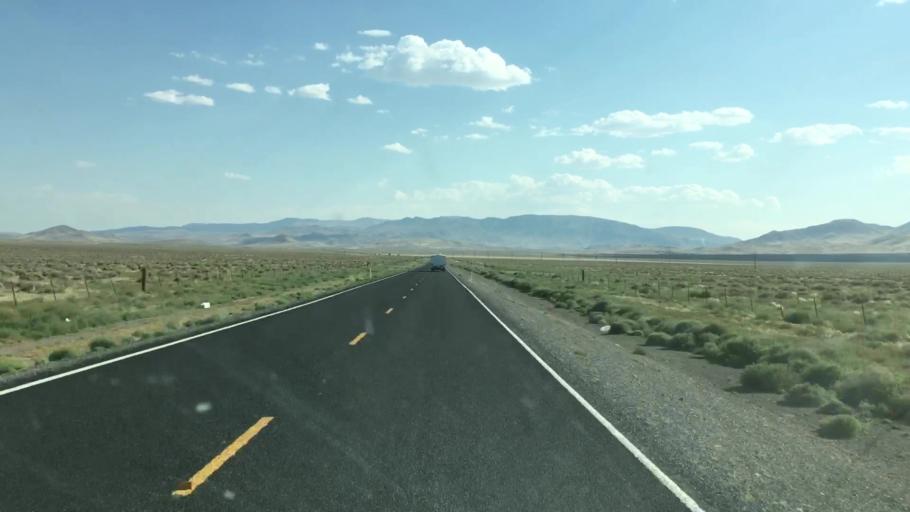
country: US
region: Nevada
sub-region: Lyon County
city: Fernley
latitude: 39.6955
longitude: -119.3349
